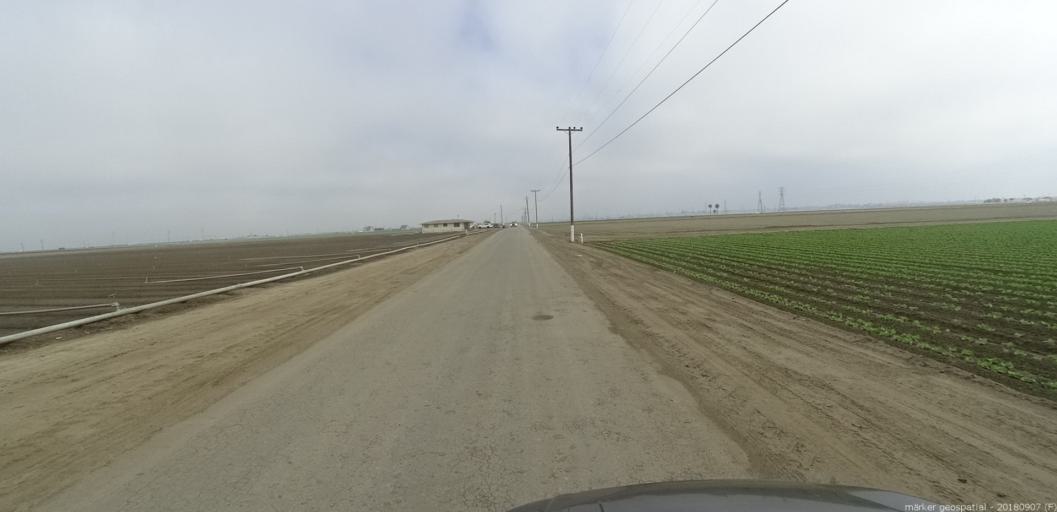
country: US
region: California
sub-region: Monterey County
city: Boronda
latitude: 36.6691
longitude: -121.7057
